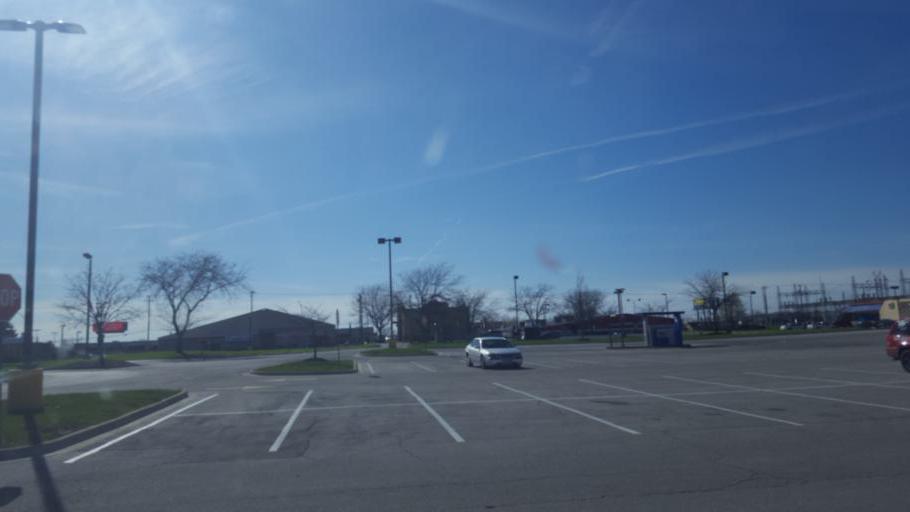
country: US
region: Ohio
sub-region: Franklin County
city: Dublin
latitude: 40.0661
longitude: -83.0912
